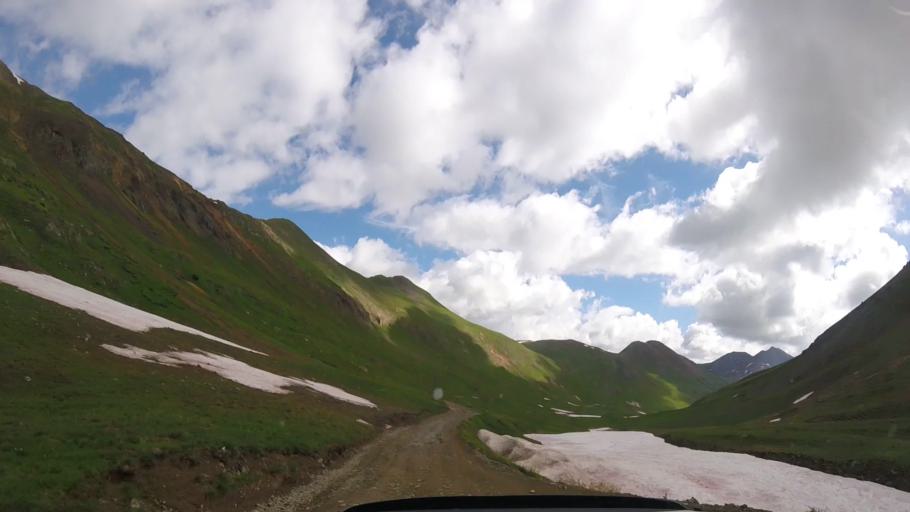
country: US
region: Colorado
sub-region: Ouray County
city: Ouray
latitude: 37.9222
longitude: -107.6120
